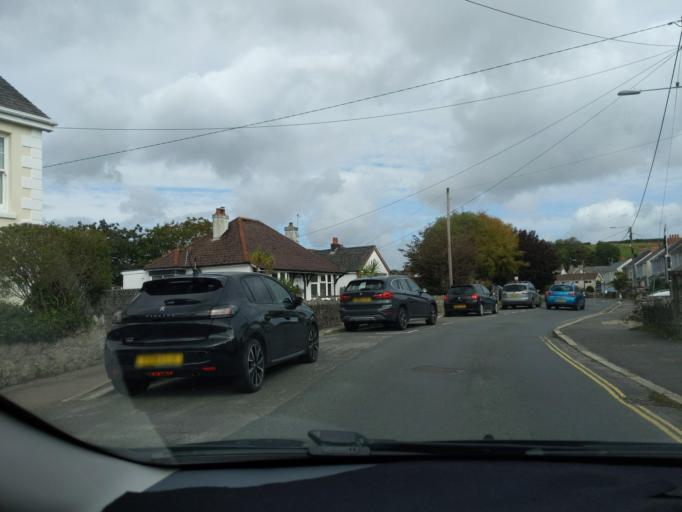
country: GB
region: England
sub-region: Cornwall
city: Par
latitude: 50.3522
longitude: -4.7030
